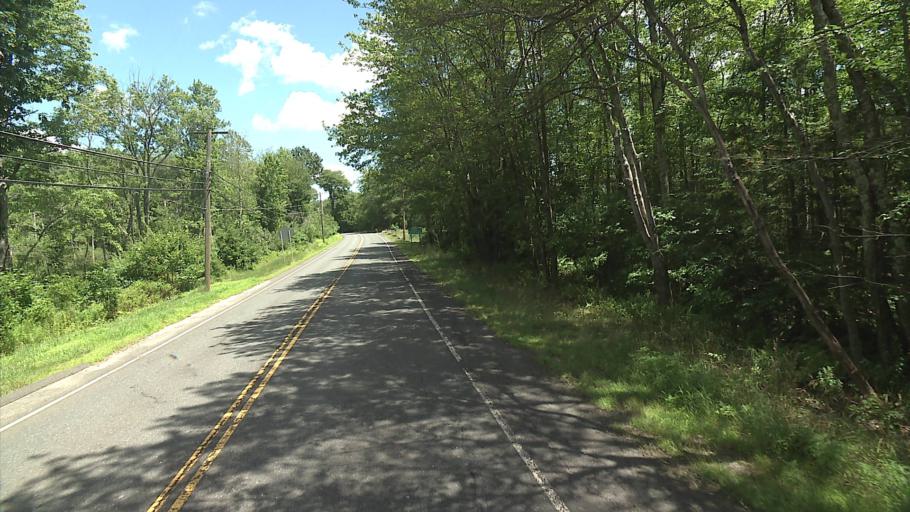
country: US
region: Connecticut
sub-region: Litchfield County
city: New Hartford Center
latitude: 41.9386
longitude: -72.9174
